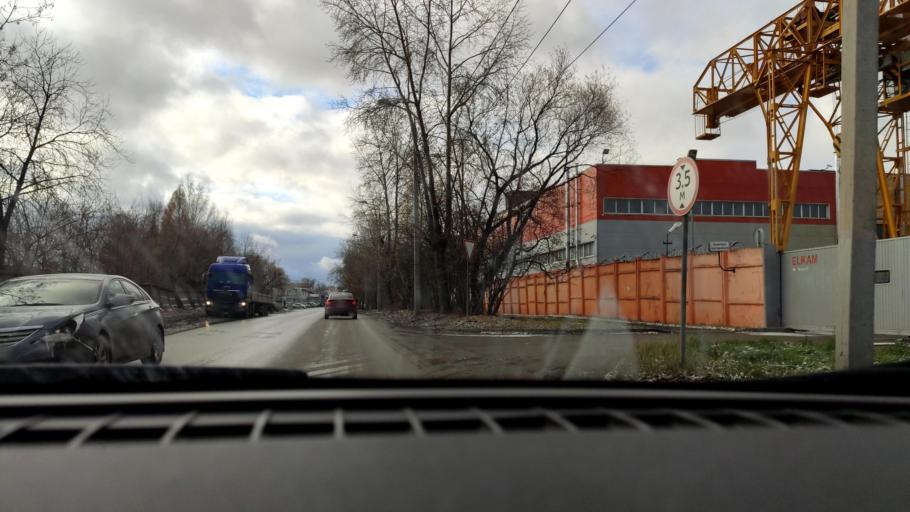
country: RU
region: Perm
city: Perm
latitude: 57.9795
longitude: 56.2700
